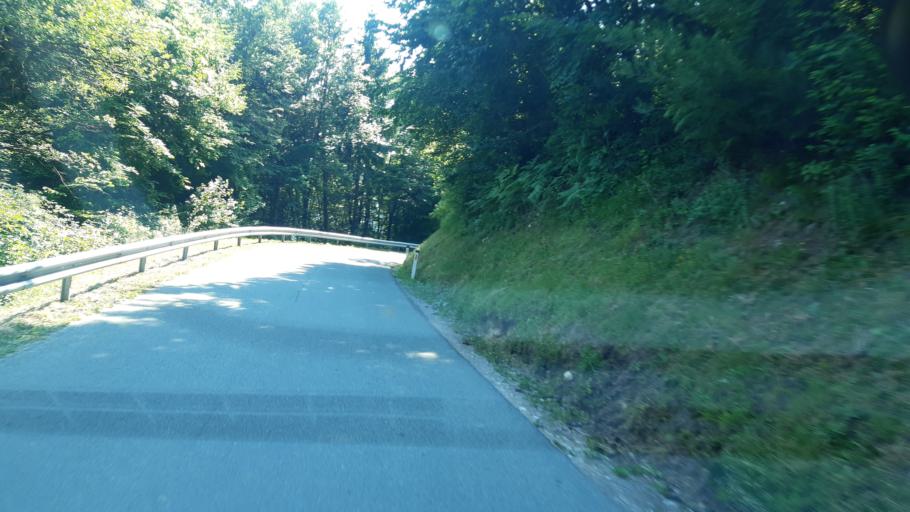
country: SI
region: Trzic
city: Bistrica pri Trzicu
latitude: 46.3595
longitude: 14.2528
